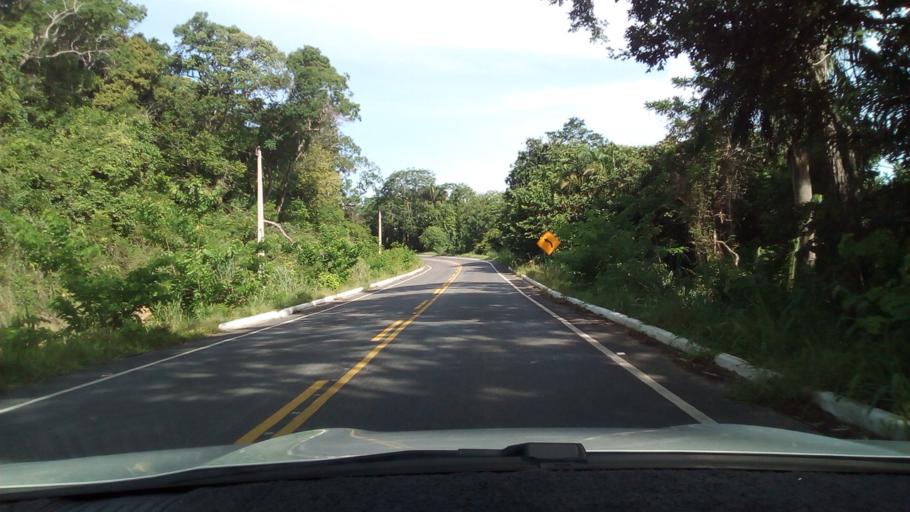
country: BR
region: Paraiba
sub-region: Santa Rita
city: Santa Rita
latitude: -7.0593
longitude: -34.9491
